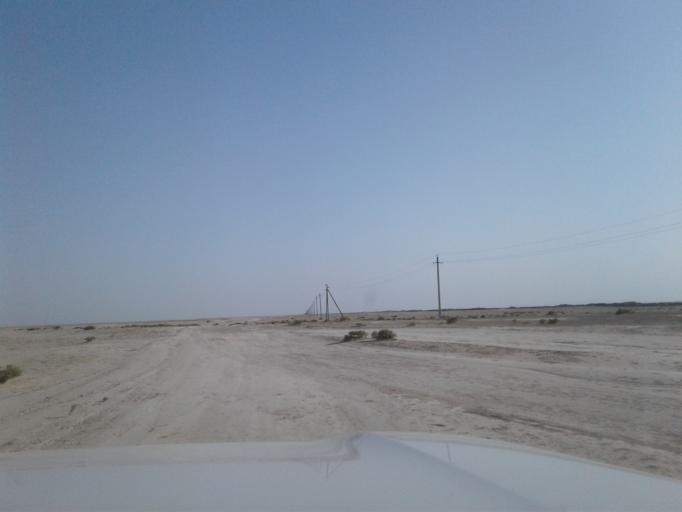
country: IR
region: Golestan
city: Aq Qayeh
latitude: 38.0584
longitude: 54.7411
